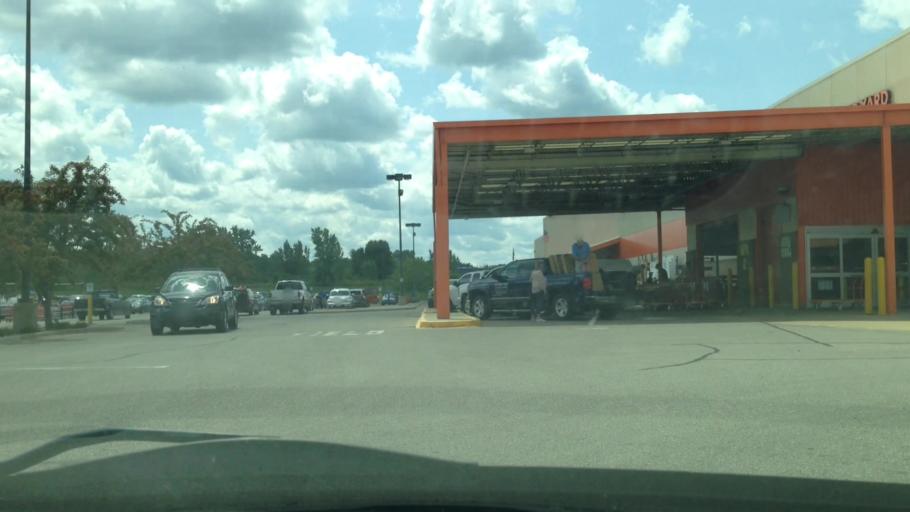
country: US
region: Minnesota
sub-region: Olmsted County
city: Rochester
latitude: 44.0646
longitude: -92.5071
